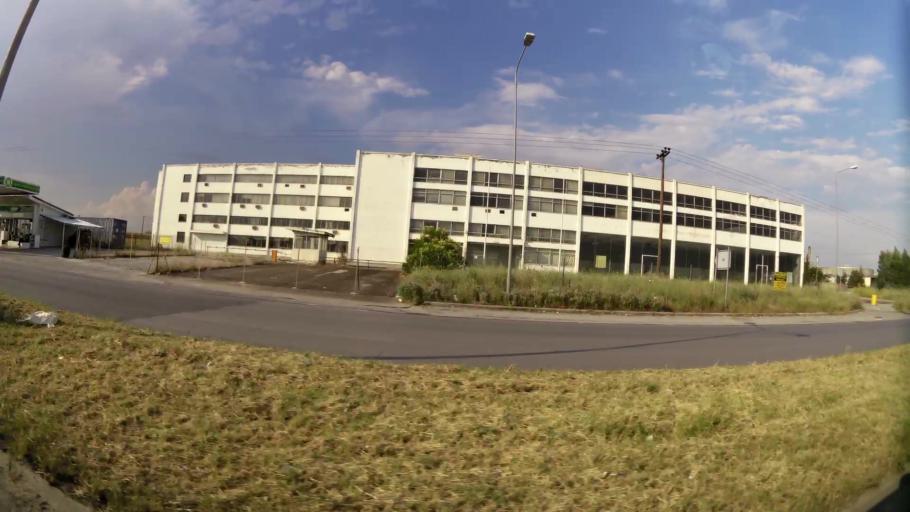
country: GR
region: Central Macedonia
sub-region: Nomos Thessalonikis
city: Diavata
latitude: 40.6785
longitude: 22.8698
